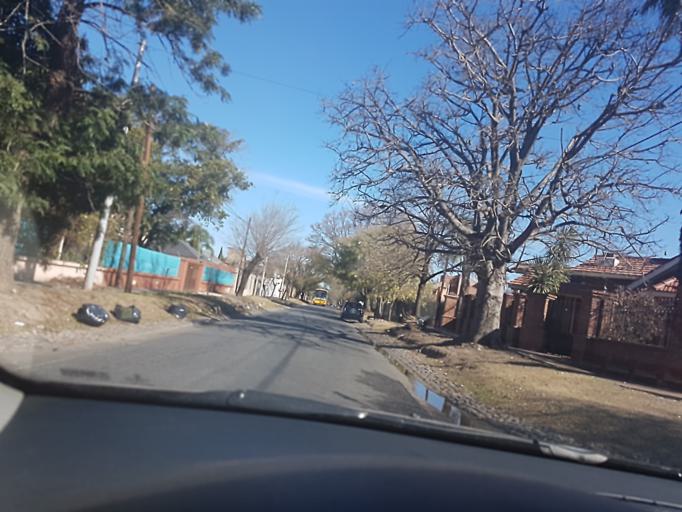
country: AR
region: Cordoba
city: Villa Allende
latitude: -31.3542
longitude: -64.2534
